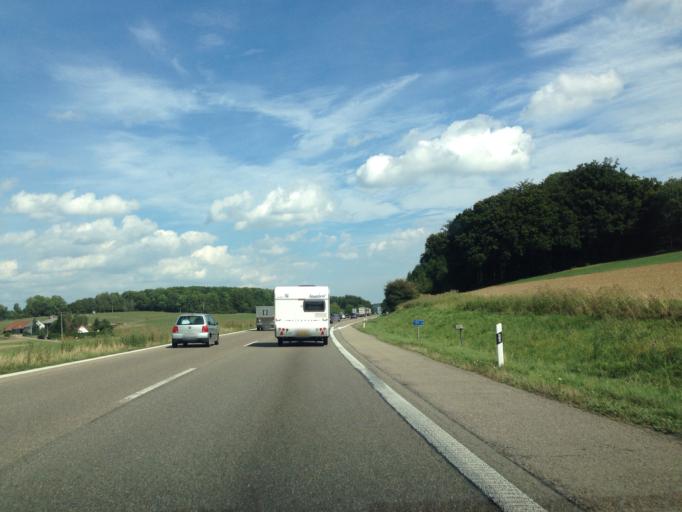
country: DE
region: Baden-Wuerttemberg
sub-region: Regierungsbezirk Stuttgart
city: Hohenstadt
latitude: 48.5505
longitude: 9.6509
